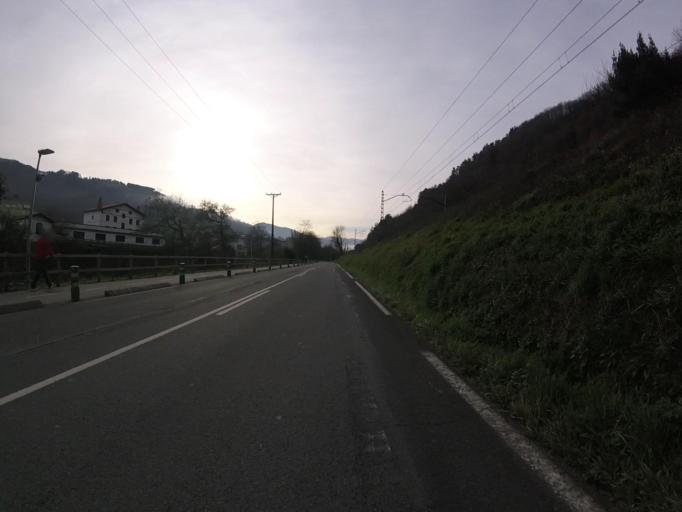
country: ES
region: Basque Country
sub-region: Provincia de Guipuzcoa
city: Anoeta
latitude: 43.1486
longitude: -2.0725
